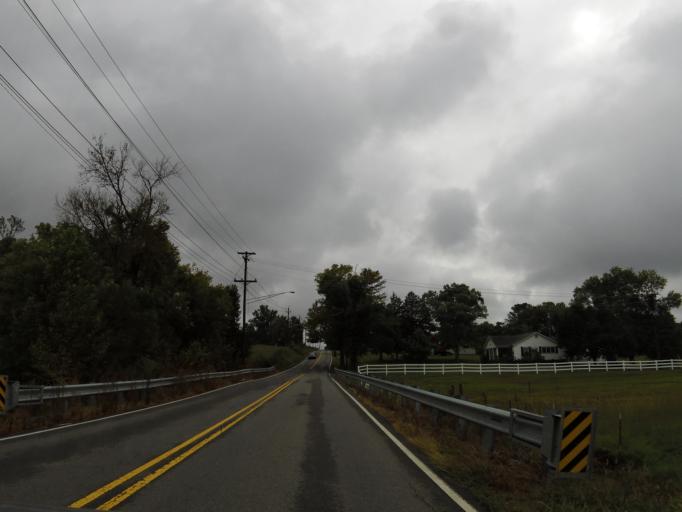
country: US
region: Tennessee
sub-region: Bradley County
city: Hopewell
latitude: 35.2080
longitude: -84.9027
